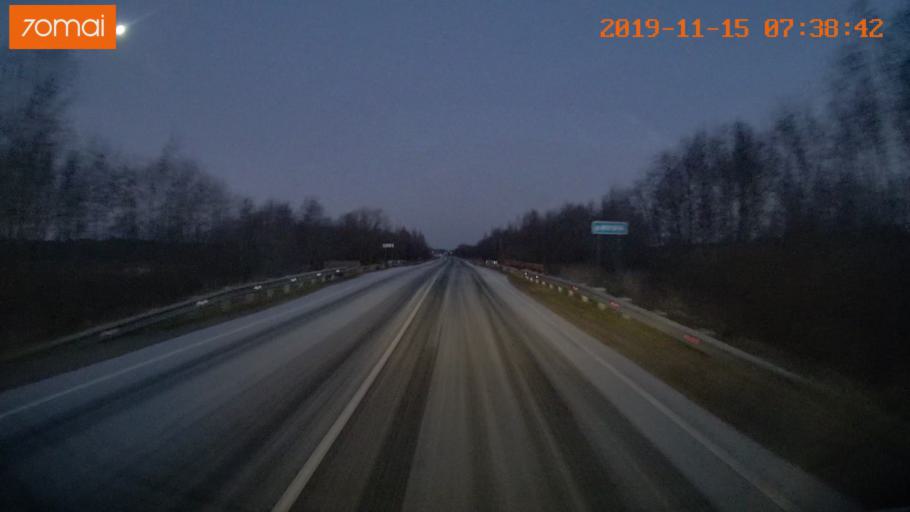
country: RU
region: Vologda
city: Sheksna
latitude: 58.7597
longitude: 38.3968
